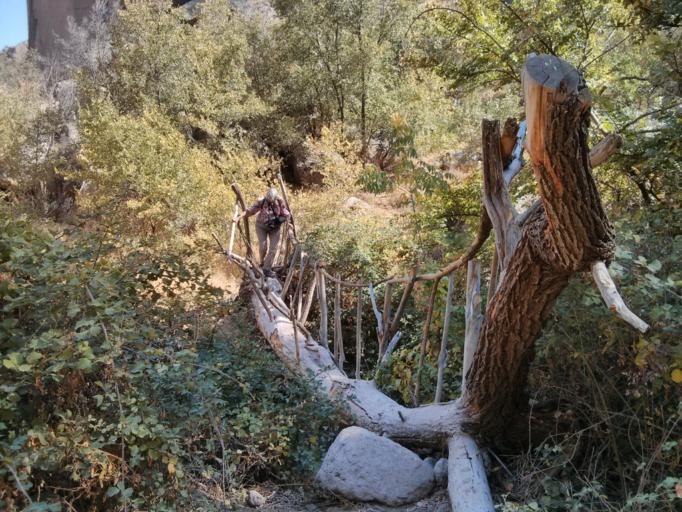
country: TR
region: Aksaray
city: Guzelyurt
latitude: 38.2539
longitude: 34.3060
